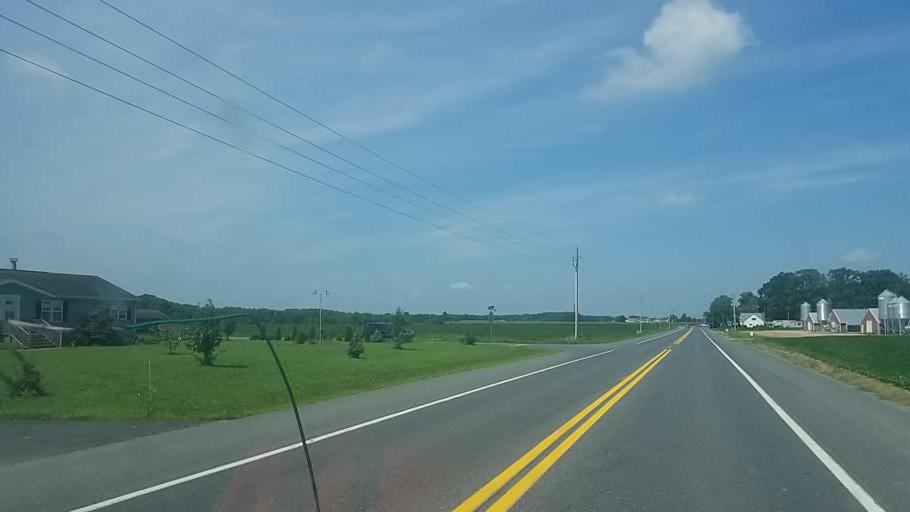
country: US
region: Delaware
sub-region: Sussex County
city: Bridgeville
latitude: 38.8253
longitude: -75.6484
